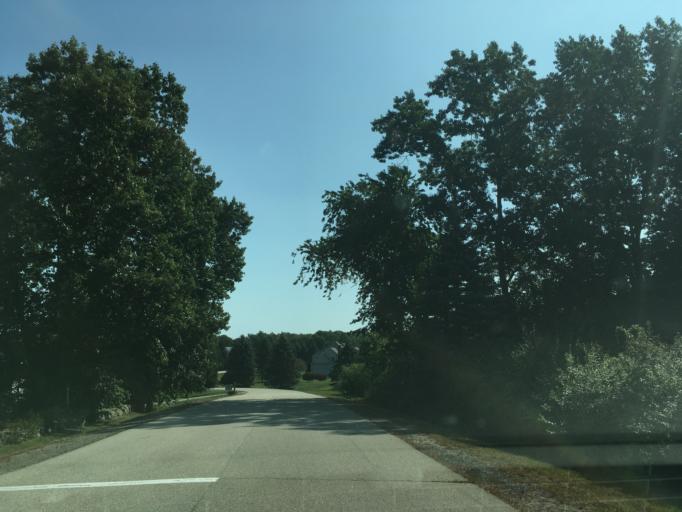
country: US
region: New Hampshire
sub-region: Rockingham County
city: Stratham Station
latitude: 43.0046
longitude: -70.8958
